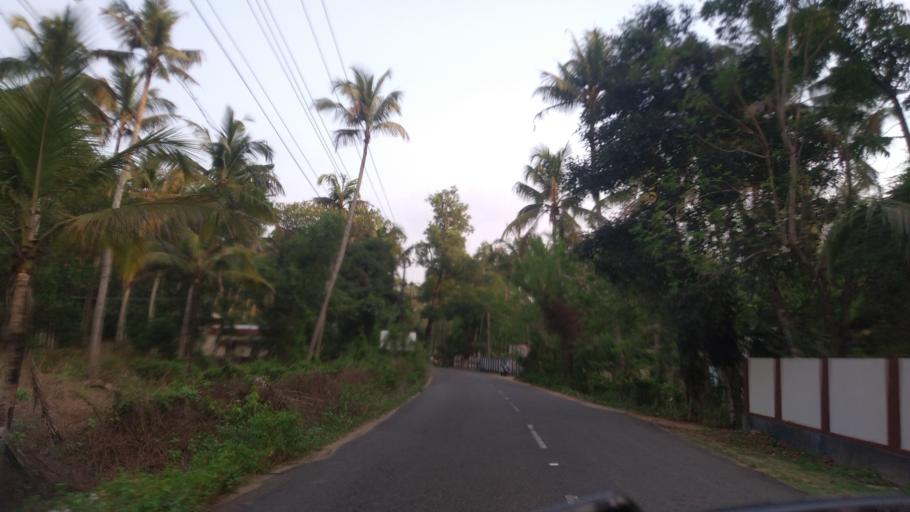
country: IN
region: Kerala
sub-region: Thrissur District
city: Irinjalakuda
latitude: 10.3236
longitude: 76.1234
